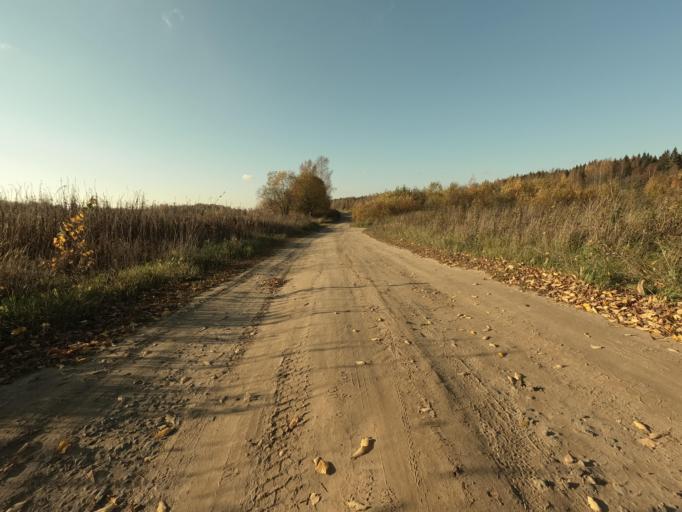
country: RU
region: Leningrad
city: Luppolovo
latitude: 60.1442
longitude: 30.2463
